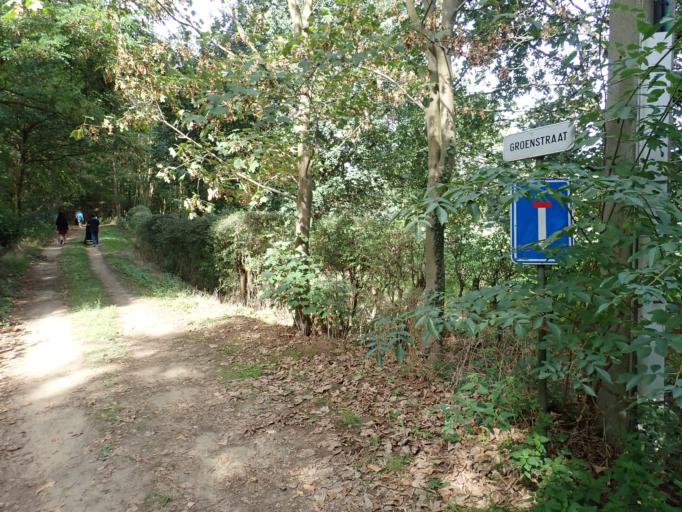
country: BE
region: Flanders
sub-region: Provincie Vlaams-Brabant
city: Oud-Heverlee
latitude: 50.8315
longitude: 4.6538
